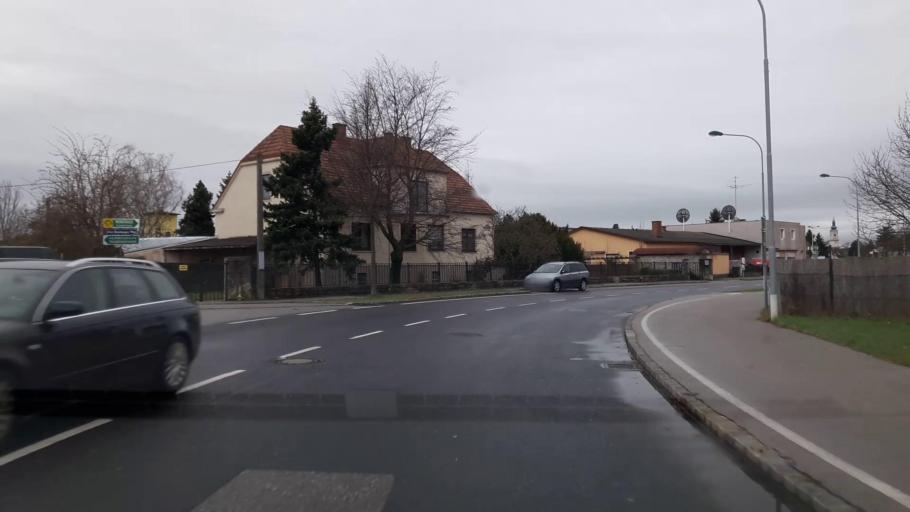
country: AT
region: Burgenland
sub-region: Politischer Bezirk Neusiedl am See
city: Bruckneudorf
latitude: 48.0333
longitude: 16.7837
